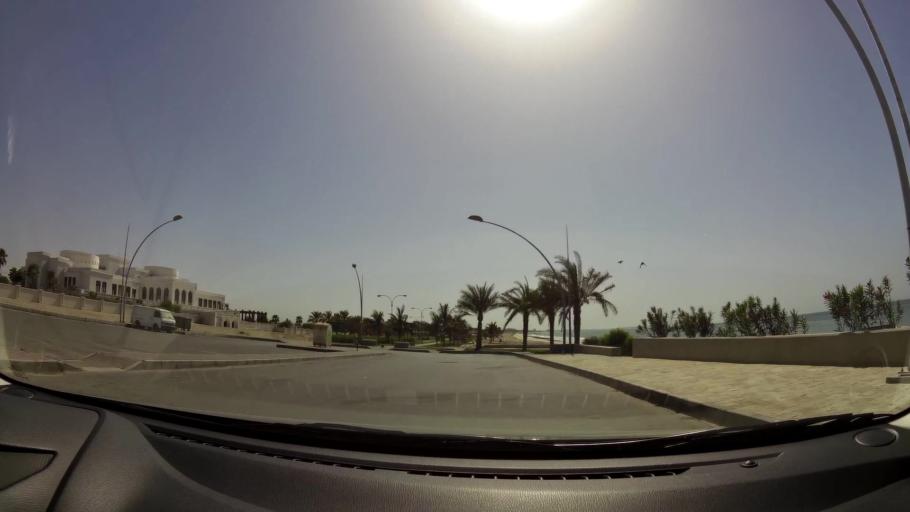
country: OM
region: Muhafazat Masqat
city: Bawshar
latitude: 23.6047
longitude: 58.3534
